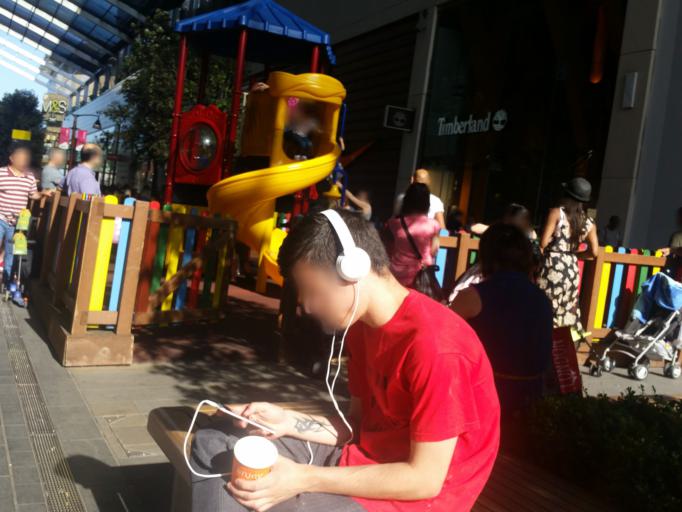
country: GB
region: England
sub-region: Greater London
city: Poplar
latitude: 51.5428
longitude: -0.0072
